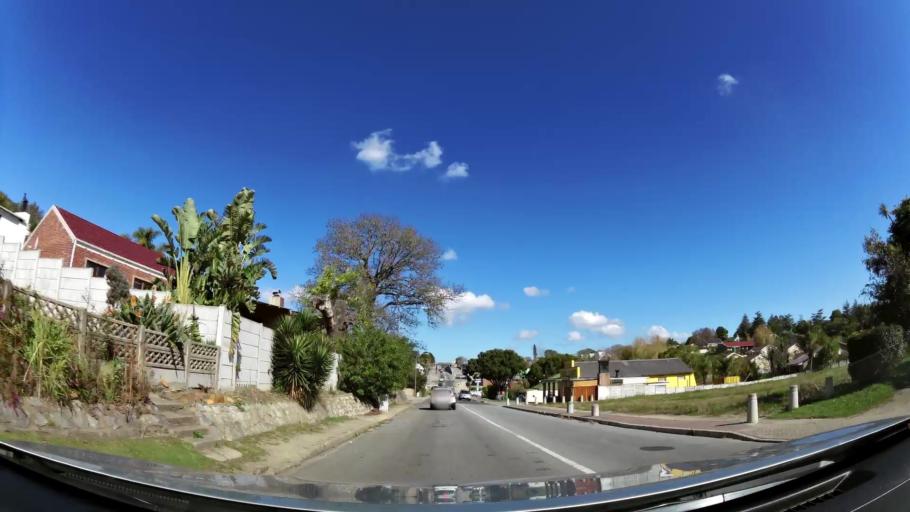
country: ZA
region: Western Cape
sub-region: Eden District Municipality
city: George
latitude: -33.9496
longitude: 22.4718
